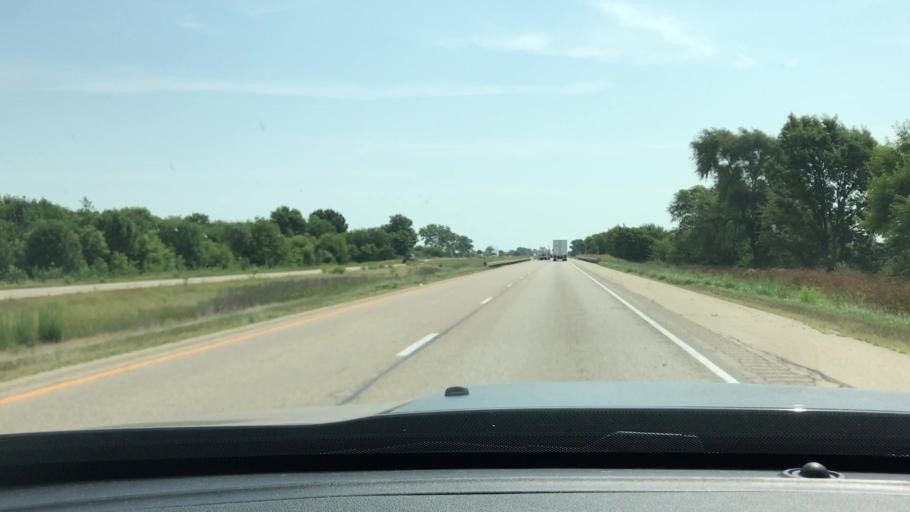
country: US
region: Illinois
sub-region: Henry County
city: Kewanee
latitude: 41.3882
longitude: -89.8317
